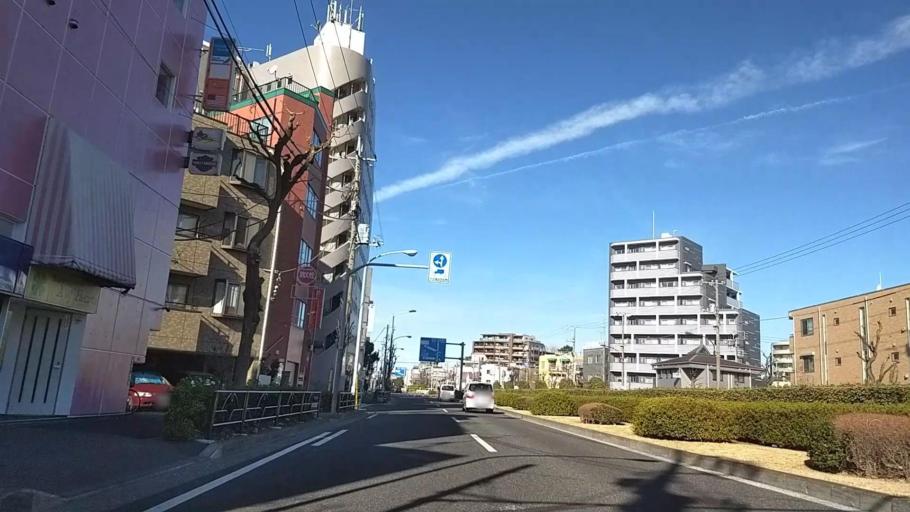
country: JP
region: Kanagawa
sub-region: Kawasaki-shi
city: Kawasaki
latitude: 35.5705
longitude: 139.6896
